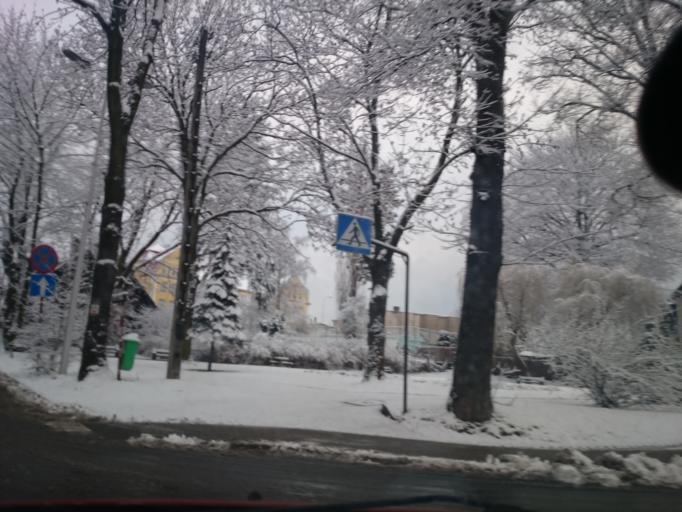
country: PL
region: Lower Silesian Voivodeship
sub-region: Powiat klodzki
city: Bystrzyca Klodzka
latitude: 50.2996
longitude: 16.6526
